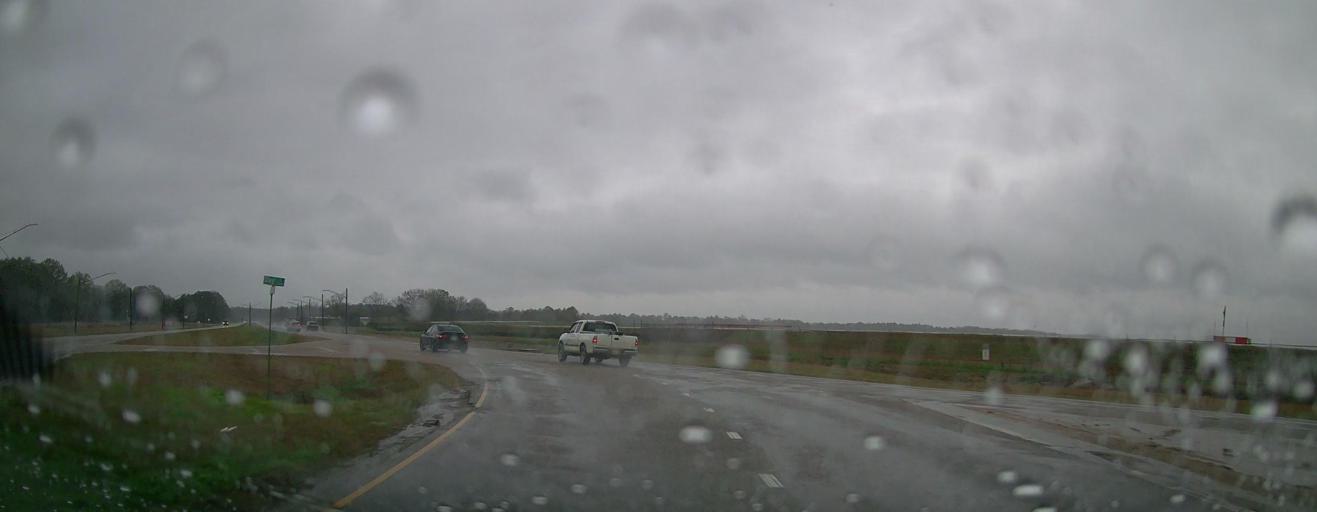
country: US
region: Alabama
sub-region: Montgomery County
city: Montgomery
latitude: 32.3687
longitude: -86.3553
